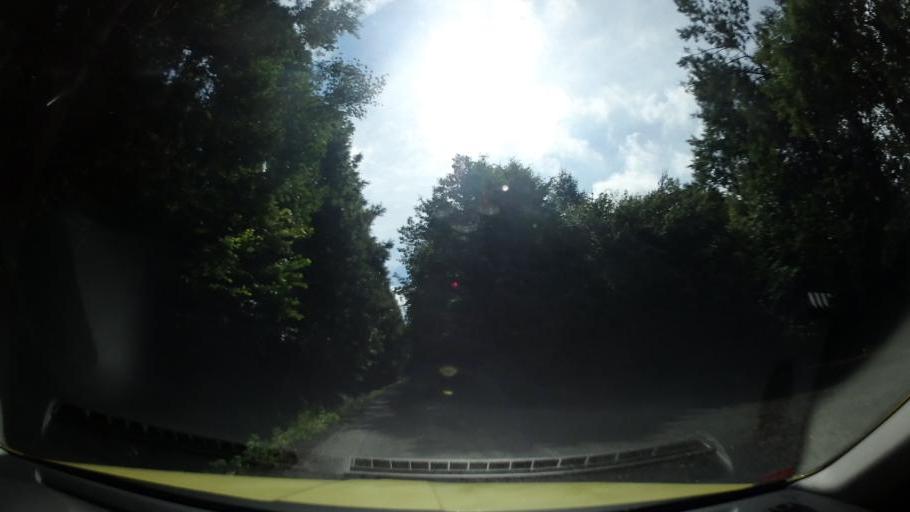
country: CZ
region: Zlin
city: Valasske Mezirici
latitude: 49.5018
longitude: 17.9995
